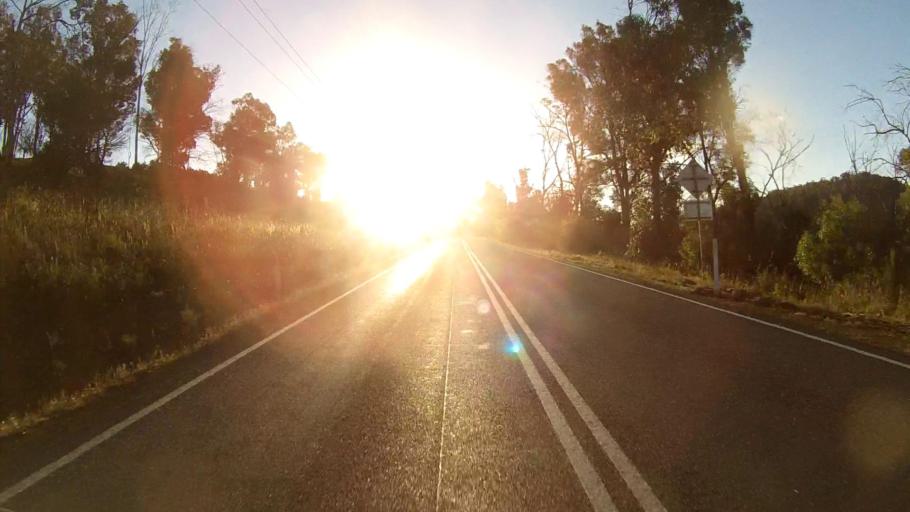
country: AU
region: Tasmania
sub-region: Sorell
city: Sorell
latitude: -42.8520
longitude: 147.8220
